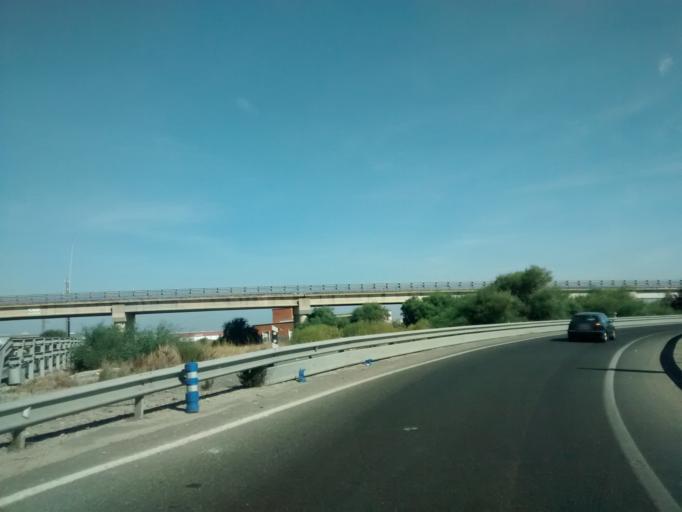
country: ES
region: Andalusia
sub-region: Provincia de Cadiz
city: San Fernando
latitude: 36.4669
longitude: -6.1648
